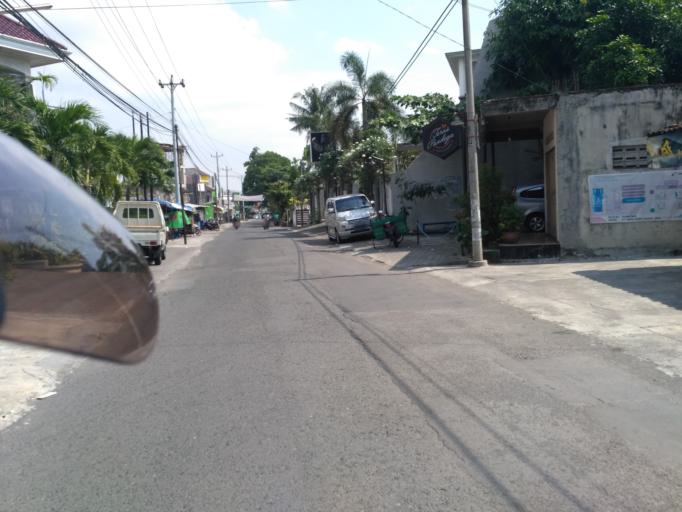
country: ID
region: Daerah Istimewa Yogyakarta
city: Melati
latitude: -7.7555
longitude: 110.3784
